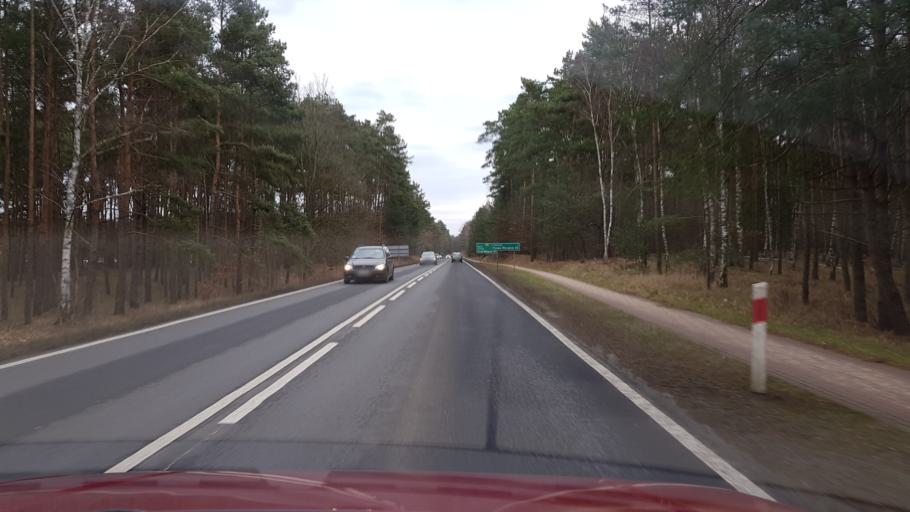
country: PL
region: West Pomeranian Voivodeship
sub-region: Powiat policki
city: Dobra
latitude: 53.5349
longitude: 14.4698
